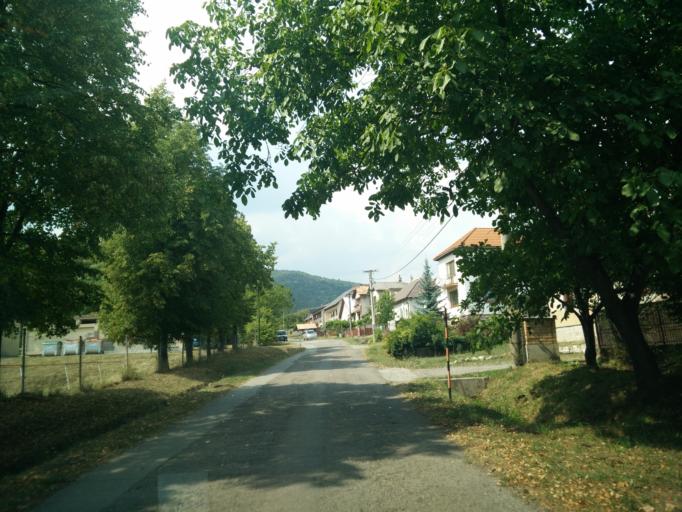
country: SK
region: Banskobystricky
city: Ziar nad Hronom
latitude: 48.5901
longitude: 18.7559
